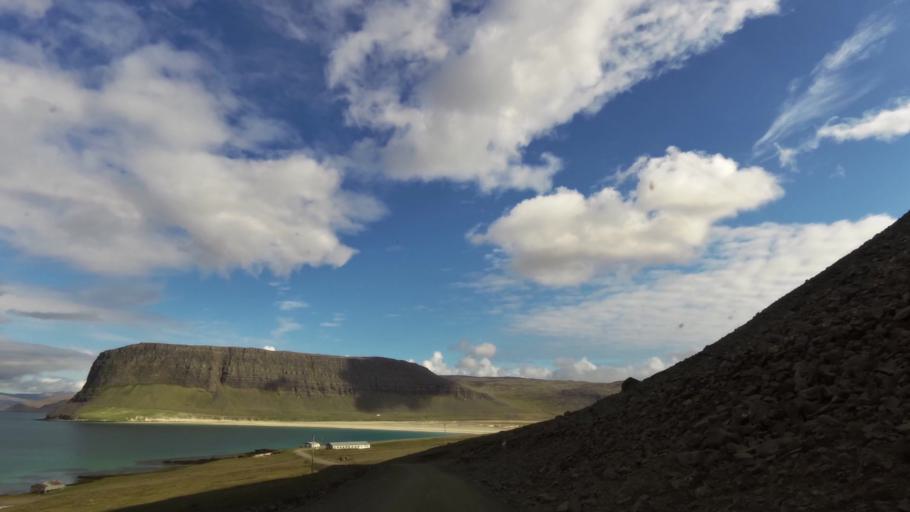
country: IS
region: West
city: Olafsvik
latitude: 65.5944
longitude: -24.1291
